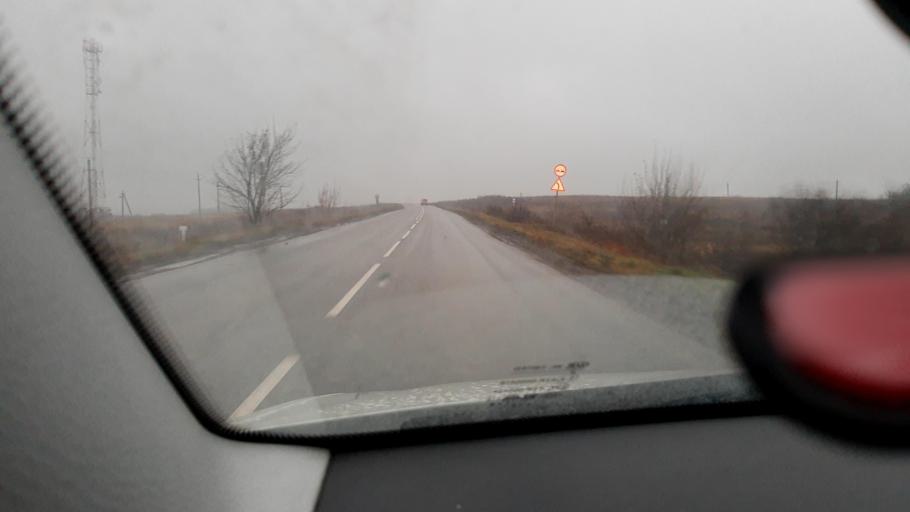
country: RU
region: Bashkortostan
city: Blagoveshchensk
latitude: 54.9015
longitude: 56.1741
